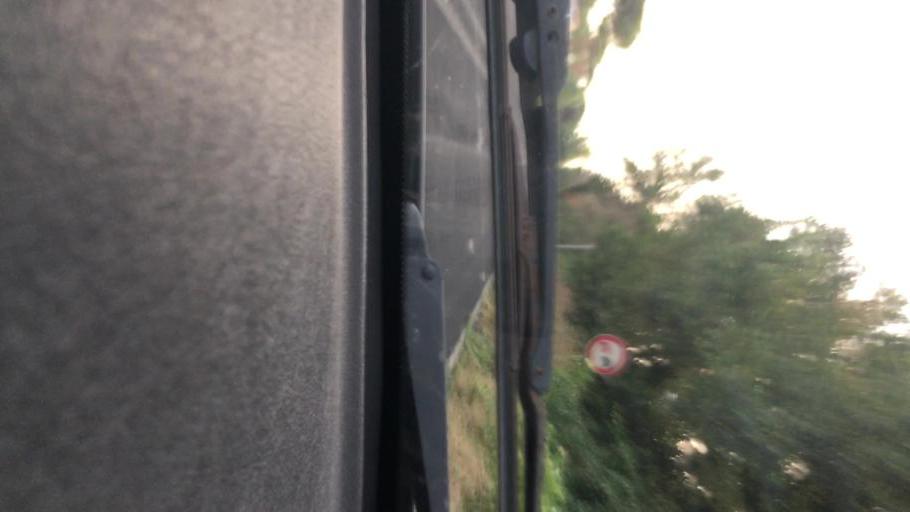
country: IT
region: Latium
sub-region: Citta metropolitana di Roma Capitale
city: Vitinia
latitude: 41.8236
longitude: 12.4413
